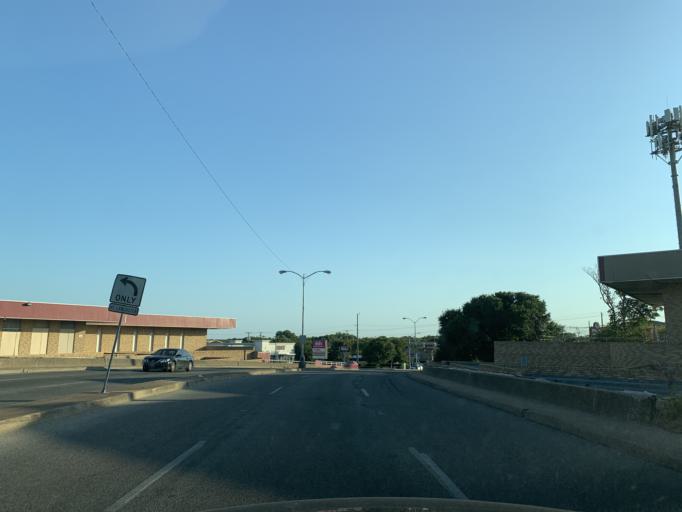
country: US
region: Texas
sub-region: Dallas County
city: Dallas
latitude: 32.7097
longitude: -96.8009
